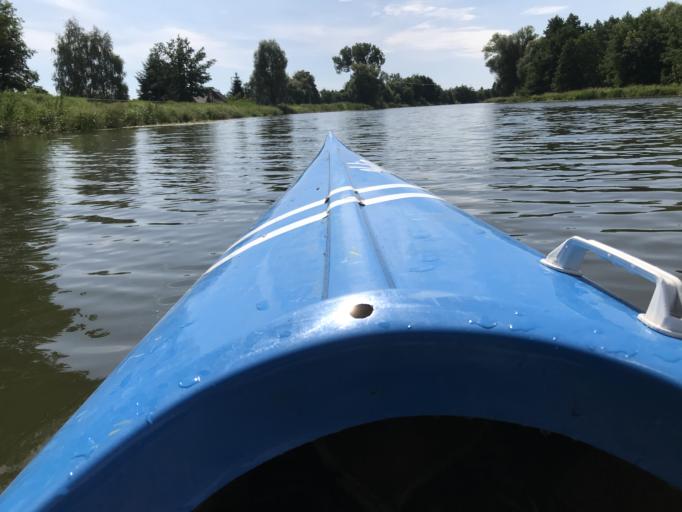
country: PL
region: Greater Poland Voivodeship
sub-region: Kalisz
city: Kalisz
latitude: 51.7506
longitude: 18.1074
